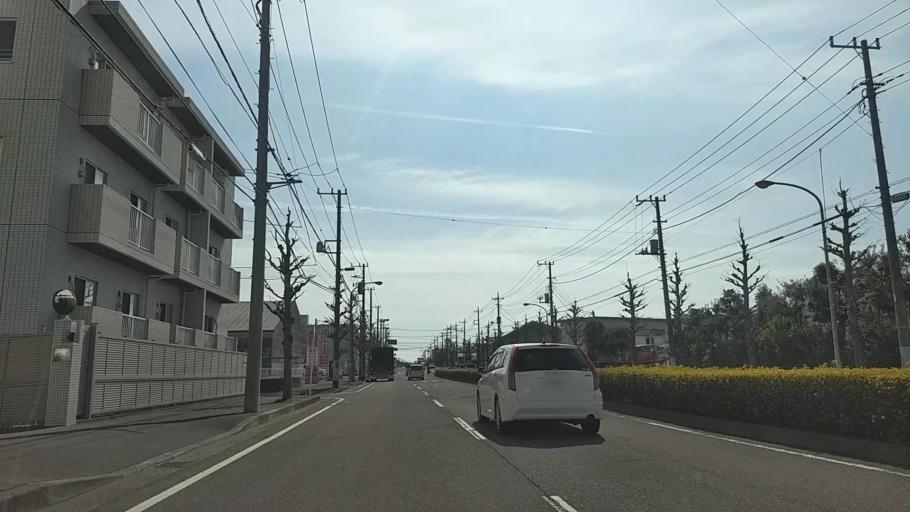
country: JP
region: Kanagawa
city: Fujisawa
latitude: 35.3912
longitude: 139.4576
